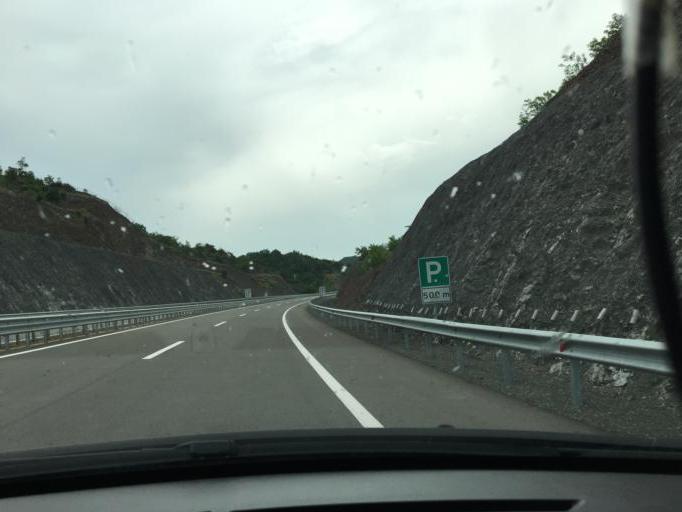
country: MK
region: Demir Kapija
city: Demir Kapija
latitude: 41.3688
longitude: 22.3413
